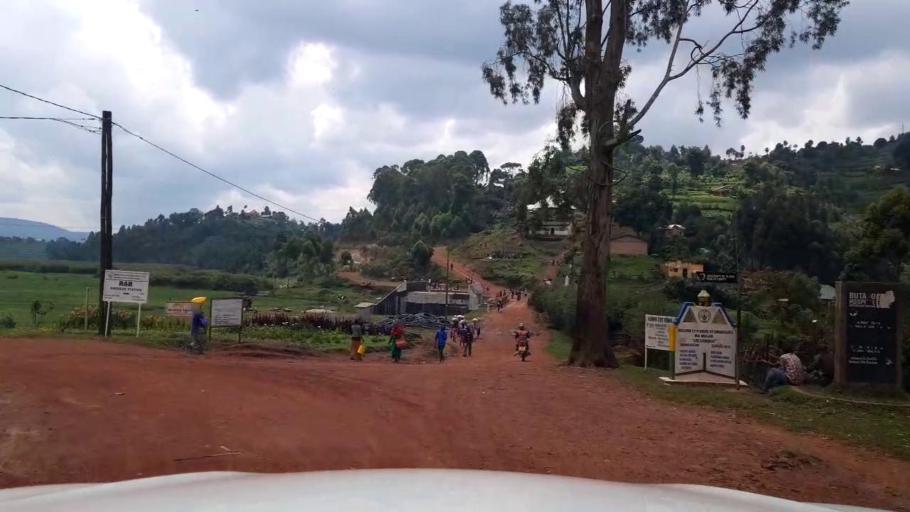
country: UG
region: Western Region
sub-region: Kisoro District
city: Kisoro
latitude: -1.4206
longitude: 29.8322
